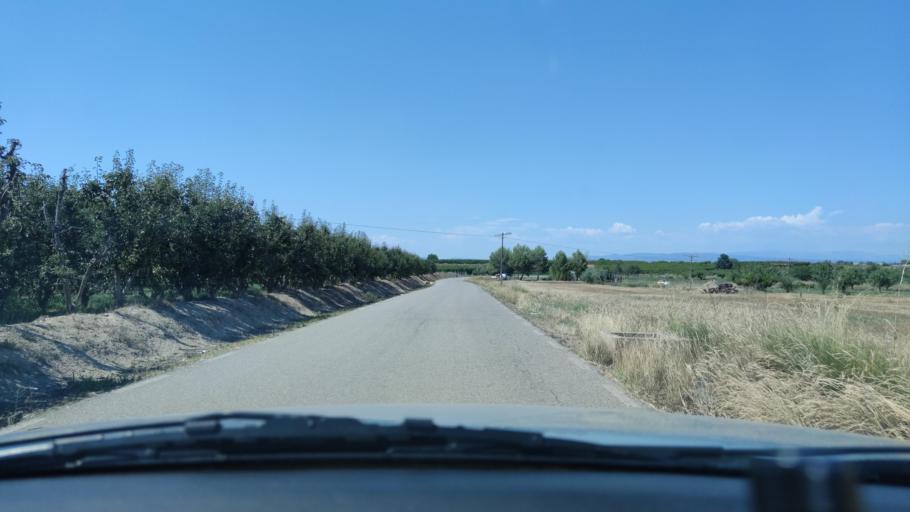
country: ES
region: Catalonia
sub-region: Provincia de Lleida
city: Torrefarrera
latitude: 41.6774
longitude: 0.6165
